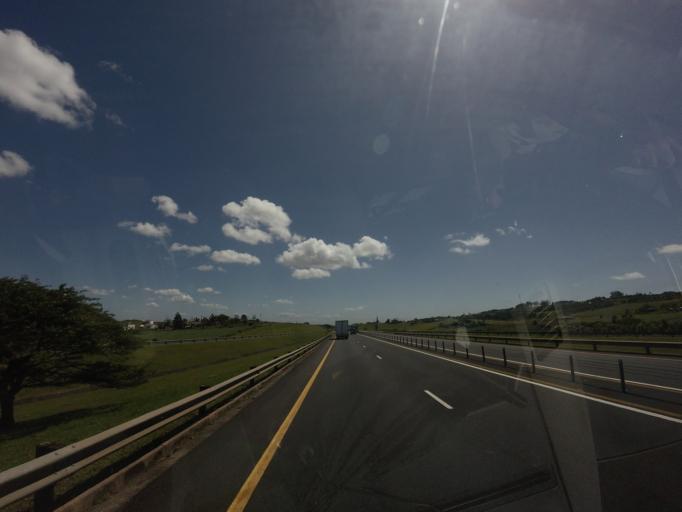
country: ZA
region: KwaZulu-Natal
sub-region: iLembe District Municipality
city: Mandeni
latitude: -29.0755
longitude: 31.6161
